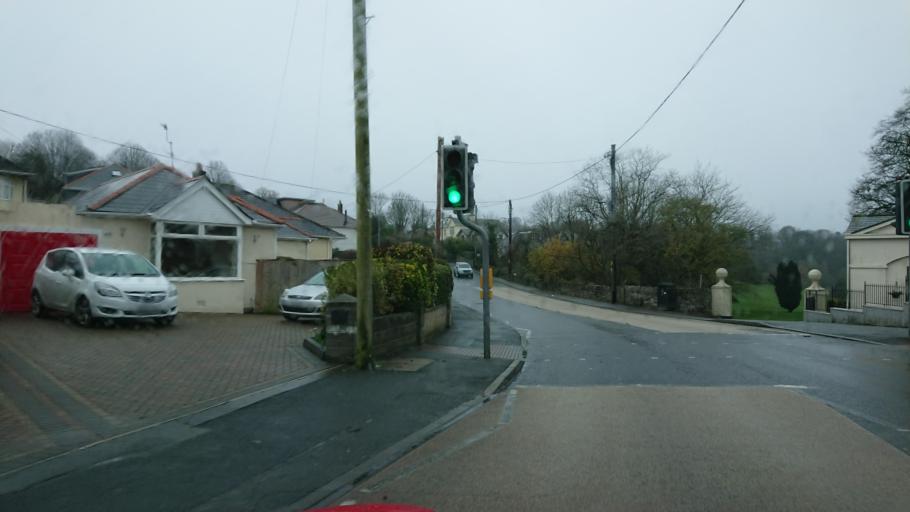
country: GB
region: England
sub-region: Plymouth
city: Plymstock
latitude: 50.3575
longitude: -4.0986
